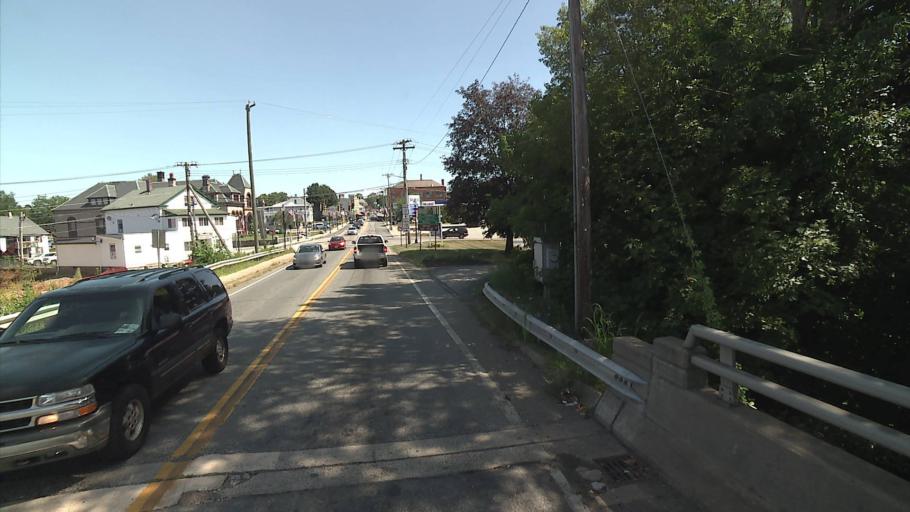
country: US
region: Connecticut
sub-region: New London County
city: Jewett City
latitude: 41.6042
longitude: -71.9846
